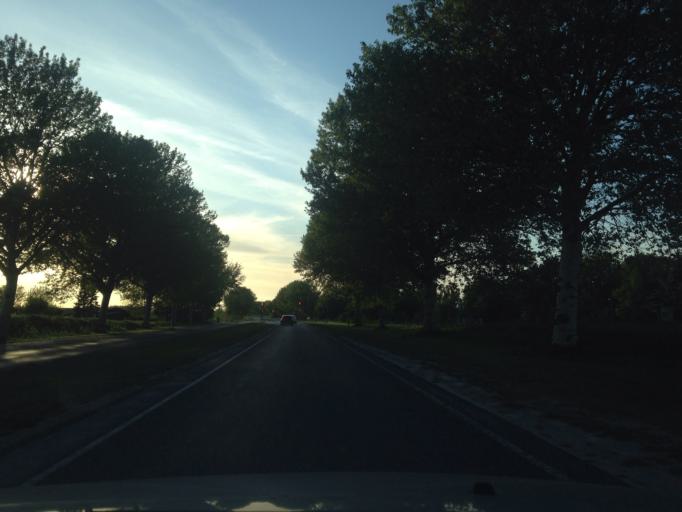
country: DK
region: Zealand
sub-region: Greve Kommune
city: Tune
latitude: 55.5976
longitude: 12.2306
